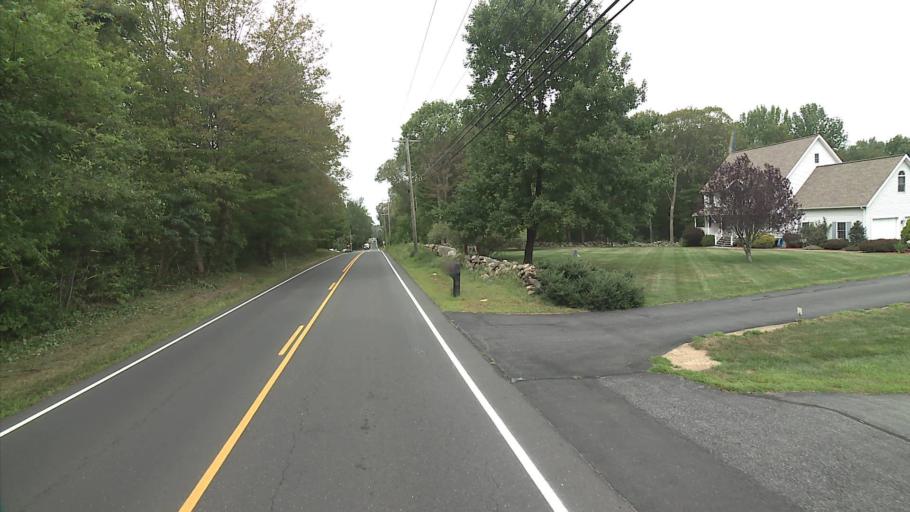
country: US
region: Connecticut
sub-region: New London County
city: Colchester
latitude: 41.5549
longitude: -72.3145
